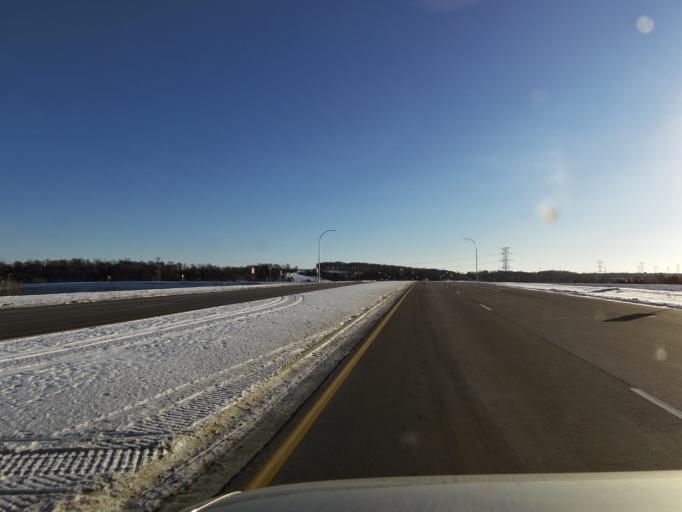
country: US
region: Minnesota
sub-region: Scott County
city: Shakopee
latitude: 44.7809
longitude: -93.5595
